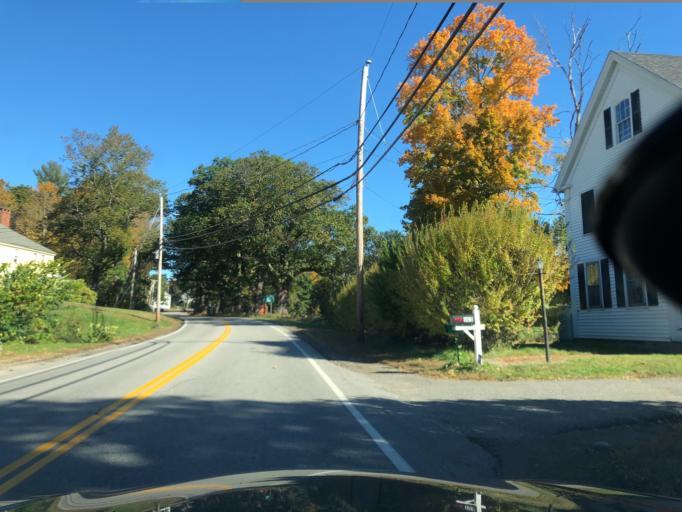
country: US
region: New Hampshire
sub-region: Rockingham County
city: Newmarket
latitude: 43.0325
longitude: -70.9433
